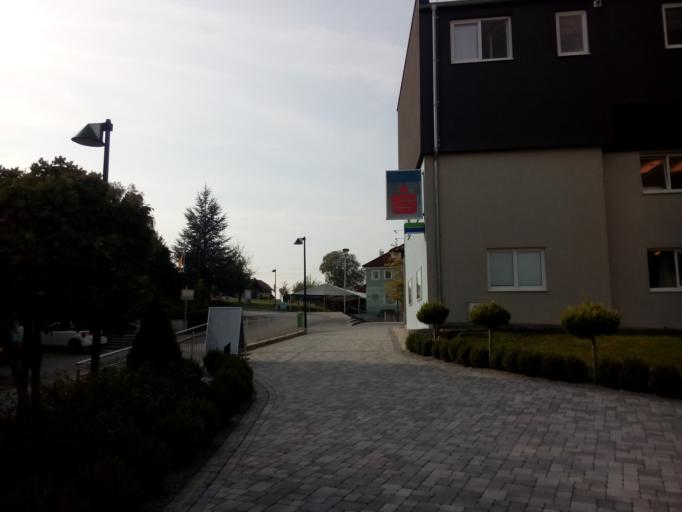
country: AT
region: Upper Austria
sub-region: Politischer Bezirk Gmunden
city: Vorchdorf
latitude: 48.0444
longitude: 13.9807
